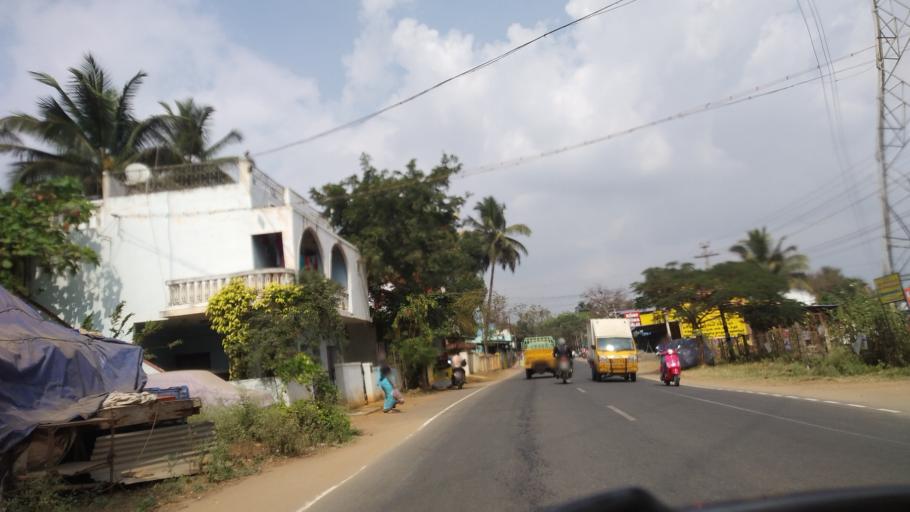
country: IN
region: Tamil Nadu
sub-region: Coimbatore
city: Perur
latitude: 10.9477
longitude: 76.9359
